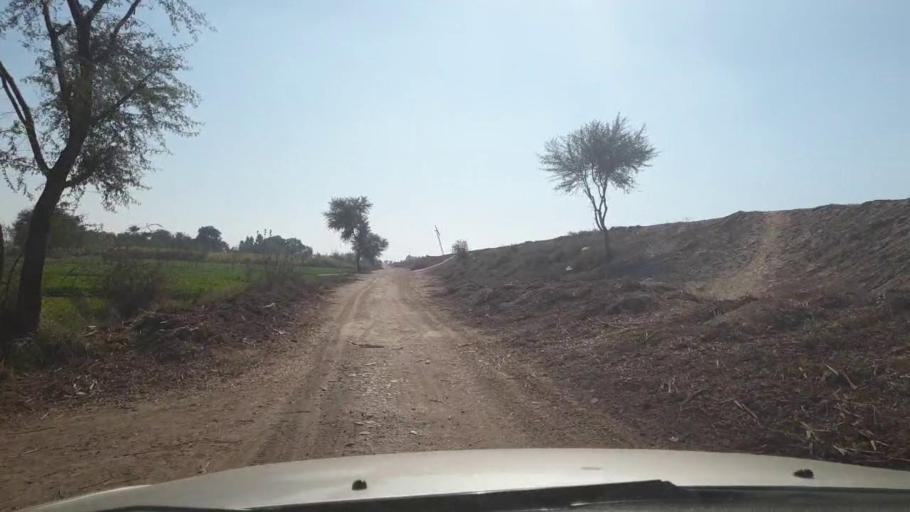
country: PK
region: Sindh
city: Ghotki
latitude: 28.0276
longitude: 69.2104
